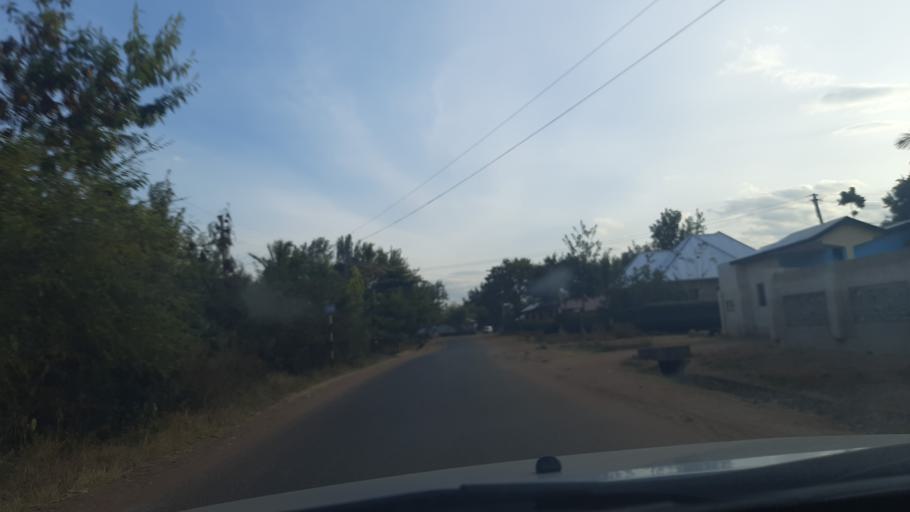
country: TZ
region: Singida
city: Singida
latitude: -4.8136
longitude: 34.7323
